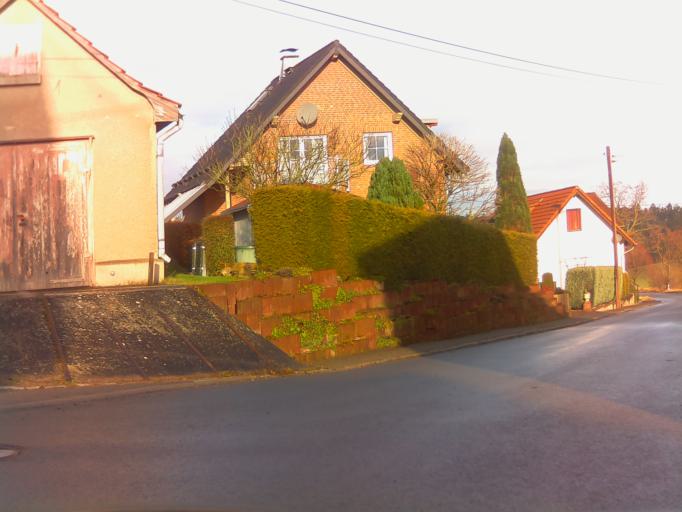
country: DE
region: Thuringia
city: Plaue
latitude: 50.8103
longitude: 10.8917
